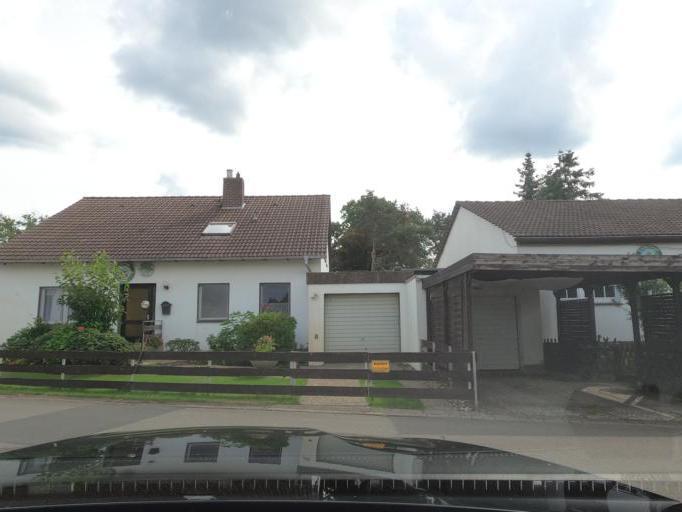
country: DE
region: Lower Saxony
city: Isernhagen Farster Bauerschaft
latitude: 52.5158
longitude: 9.9189
